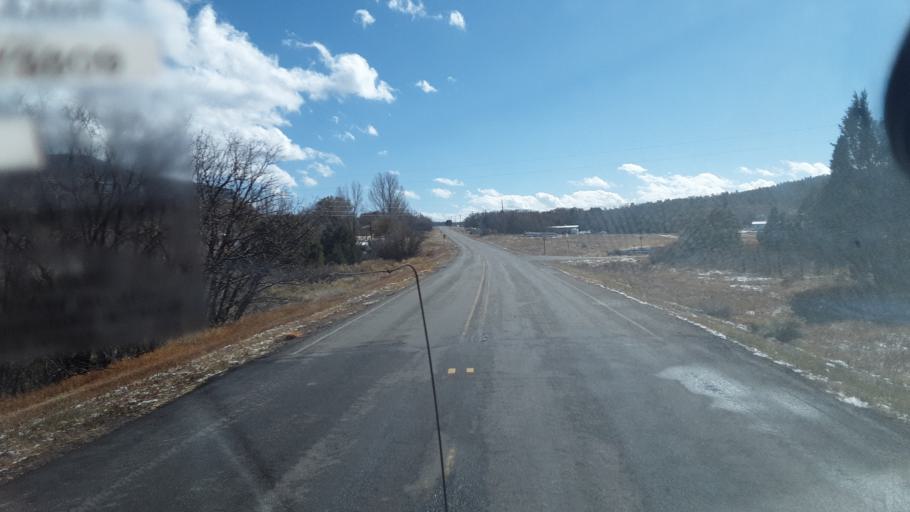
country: US
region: New Mexico
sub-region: Rio Arriba County
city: Santa Teresa
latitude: 36.2281
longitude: -106.8012
